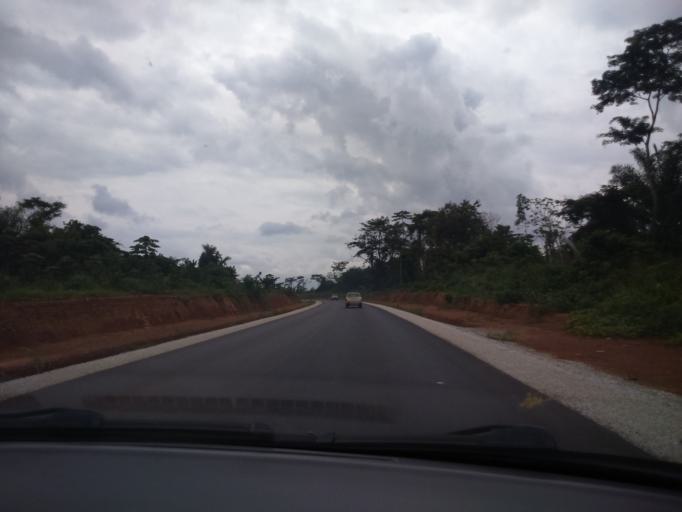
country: CI
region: Lagunes
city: Akoupe
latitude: 6.3169
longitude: -3.8316
